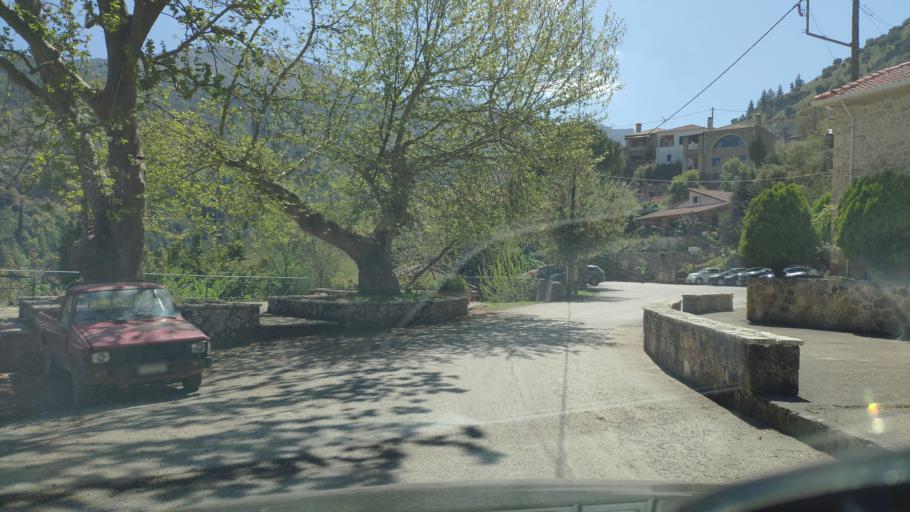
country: GR
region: West Greece
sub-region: Nomos Achaias
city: Aiyira
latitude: 38.0664
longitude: 22.3388
